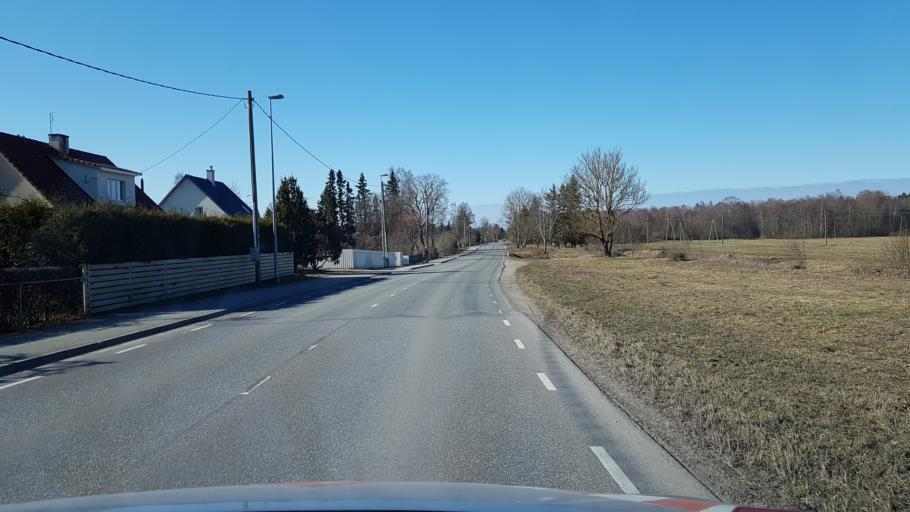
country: EE
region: Laeaene-Virumaa
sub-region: Haljala vald
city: Haljala
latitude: 59.4348
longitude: 26.2662
